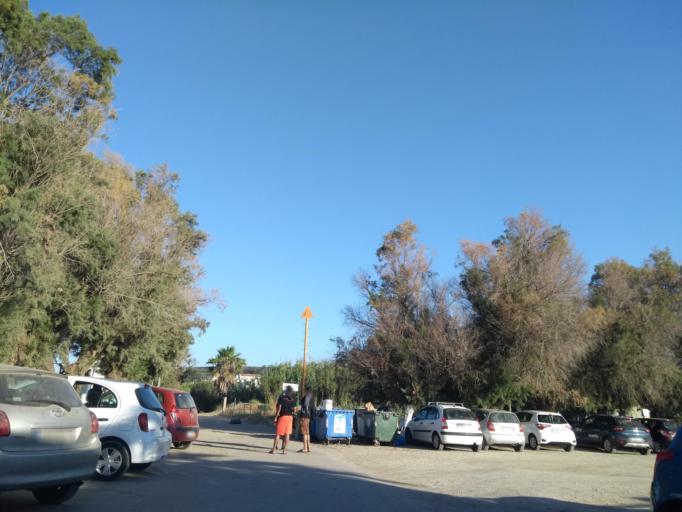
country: GR
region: Crete
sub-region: Nomos Chanias
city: Kalivai
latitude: 35.4635
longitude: 24.1582
